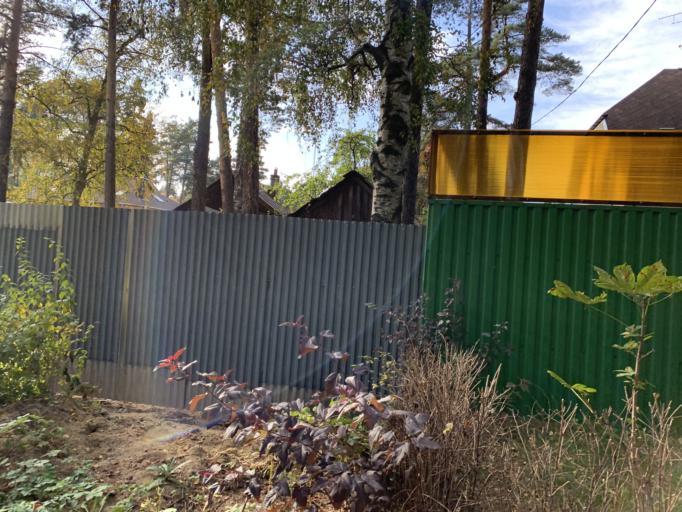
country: RU
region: Moskovskaya
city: Mamontovka
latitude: 55.9876
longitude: 37.8316
